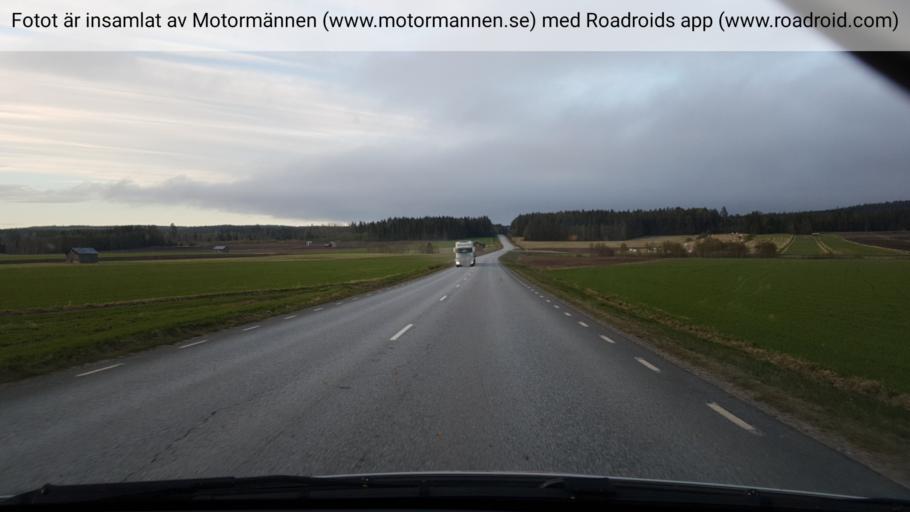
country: SE
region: Vaesterbotten
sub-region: Umea Kommun
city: Roback
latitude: 63.7757
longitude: 20.0602
